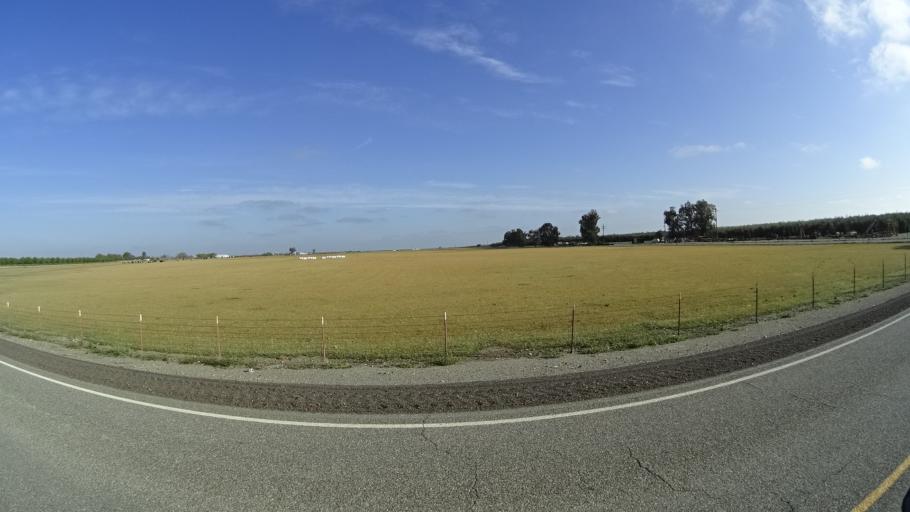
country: US
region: California
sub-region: Glenn County
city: Willows
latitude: 39.5820
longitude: -122.1619
